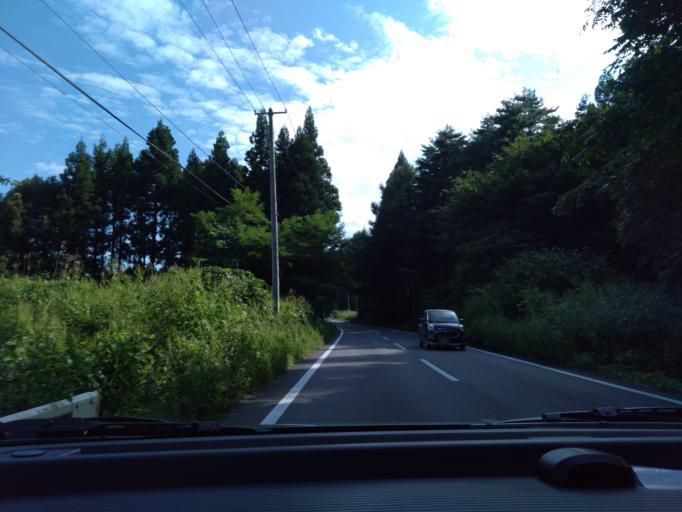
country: JP
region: Iwate
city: Morioka-shi
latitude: 39.5866
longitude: 141.0881
